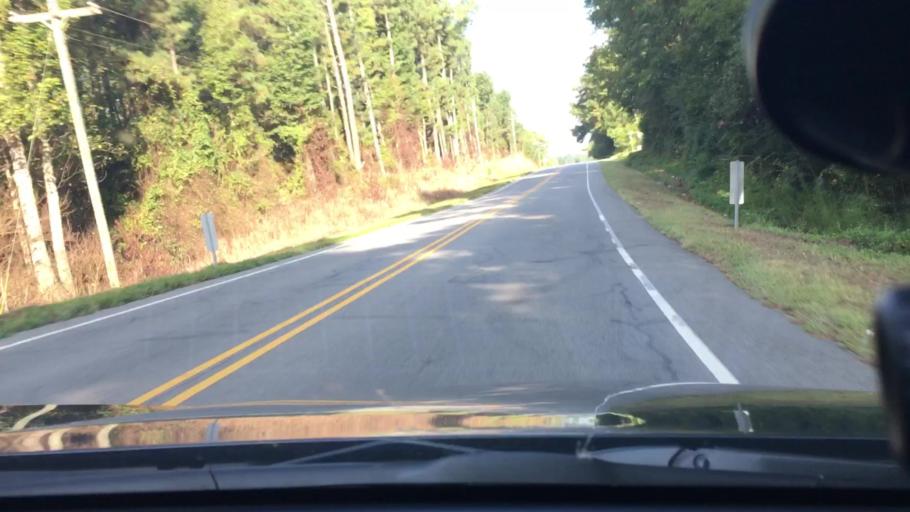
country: US
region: North Carolina
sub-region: Edgecombe County
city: Pinetops
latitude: 35.7827
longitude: -77.6154
